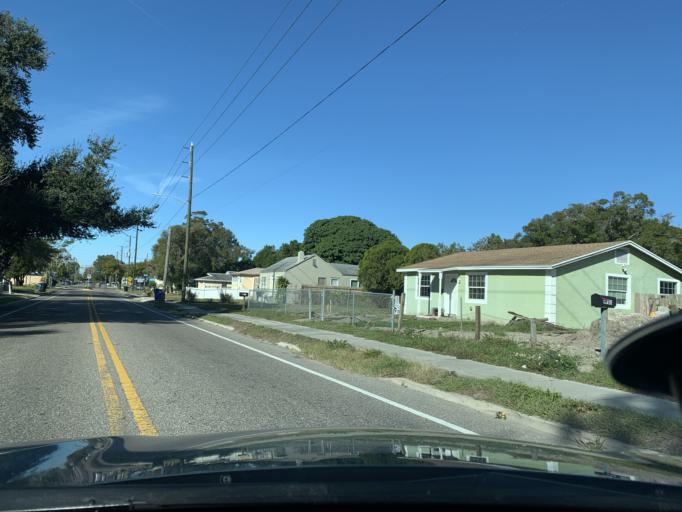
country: US
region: Florida
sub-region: Pinellas County
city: Gulfport
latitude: 27.7556
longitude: -82.6977
